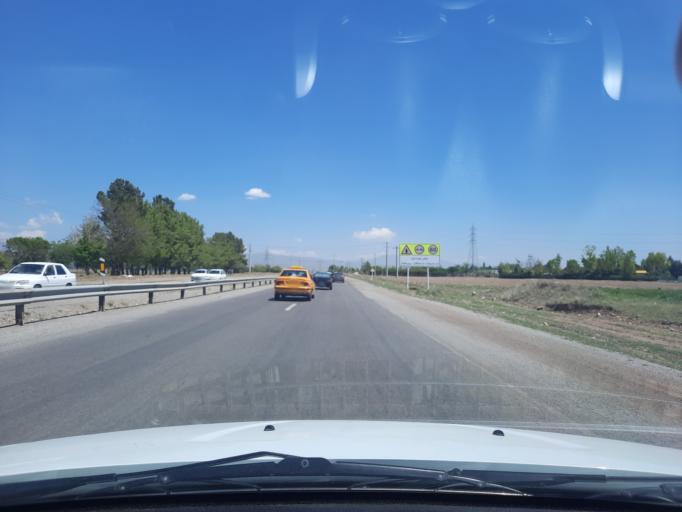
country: IR
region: Qazvin
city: Qazvin
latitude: 36.2662
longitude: 50.0745
